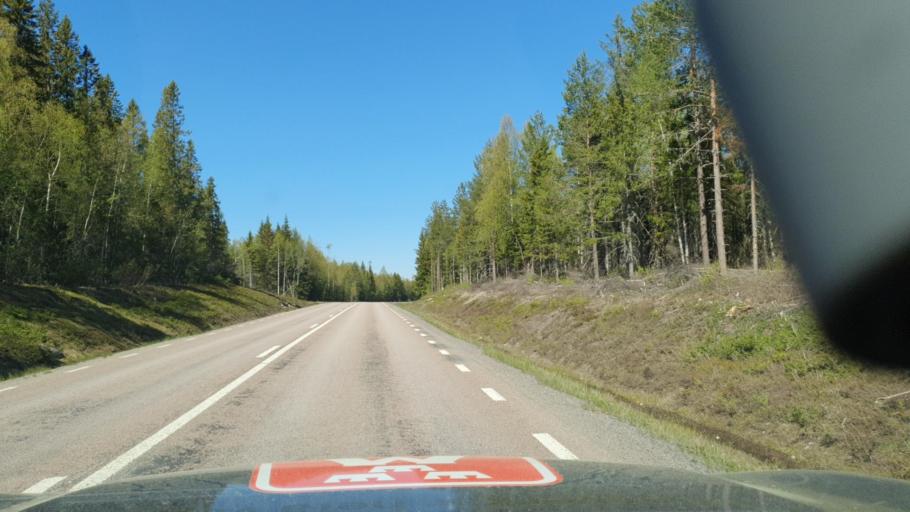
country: SE
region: Vaesternorrland
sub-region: OErnskoeldsviks Kommun
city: Ornskoldsvik
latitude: 63.4048
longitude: 18.6535
